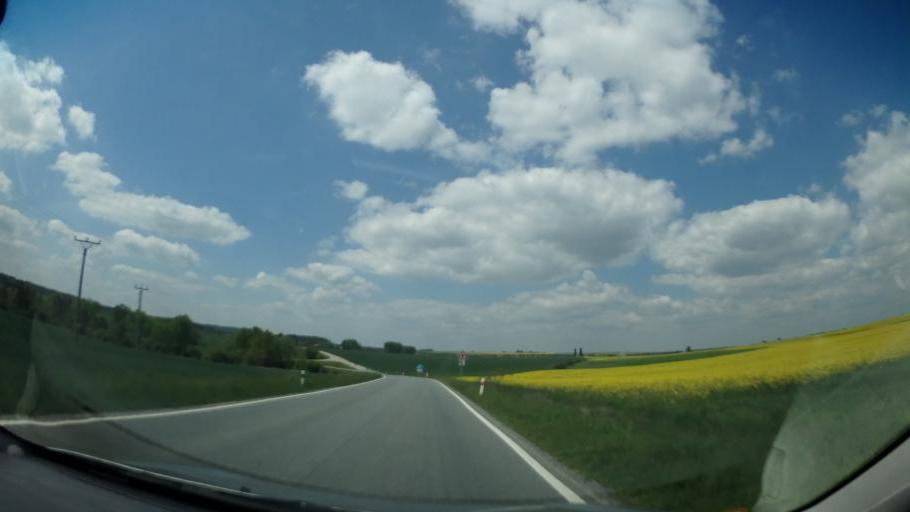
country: CZ
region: Vysocina
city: Hrotovice
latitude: 49.1804
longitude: 16.0786
